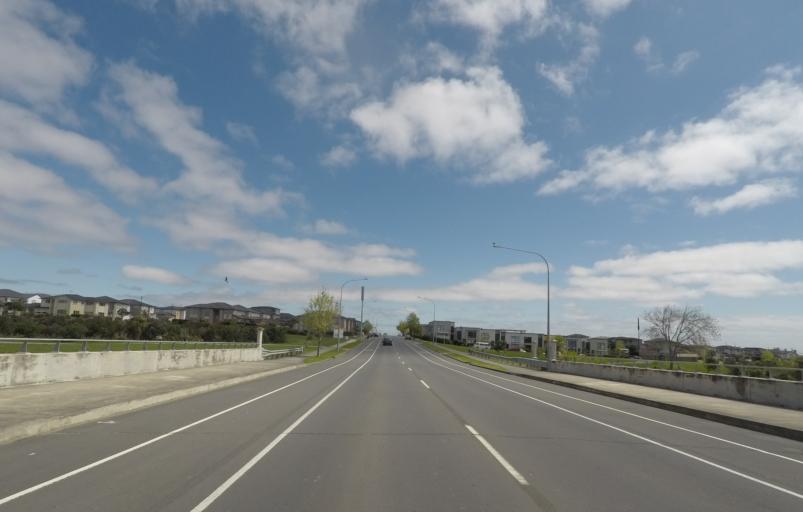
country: NZ
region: Auckland
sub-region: Auckland
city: Manukau City
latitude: -36.9740
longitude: 174.9165
